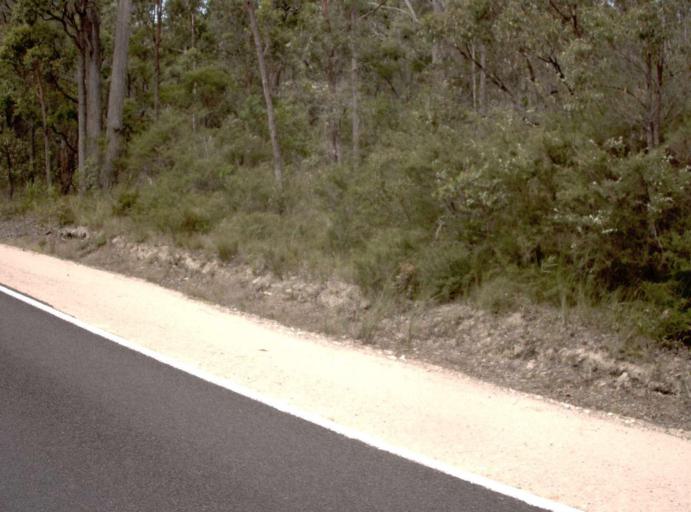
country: AU
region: New South Wales
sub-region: Bega Valley
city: Eden
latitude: -37.4377
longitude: 149.6448
